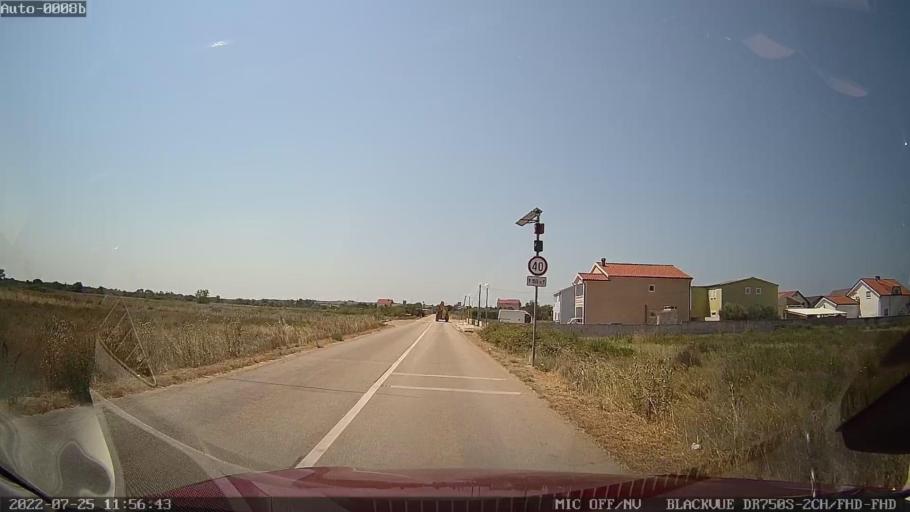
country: HR
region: Zadarska
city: Vrsi
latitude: 44.2476
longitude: 15.2166
